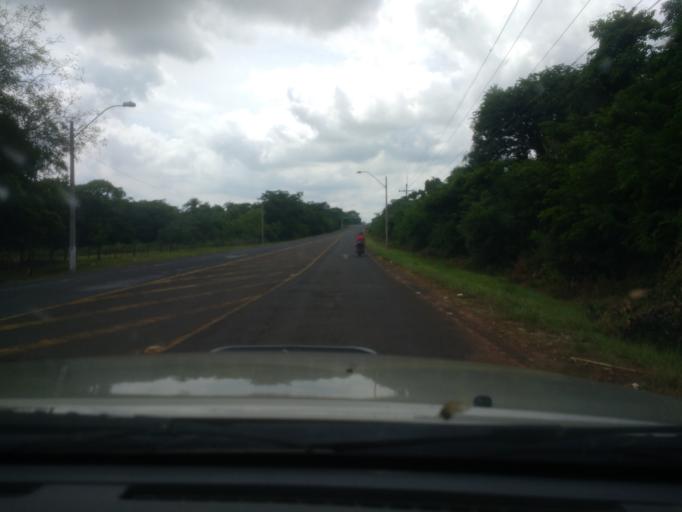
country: PY
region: San Pedro
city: Puerto Rosario
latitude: -24.4247
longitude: -57.0840
